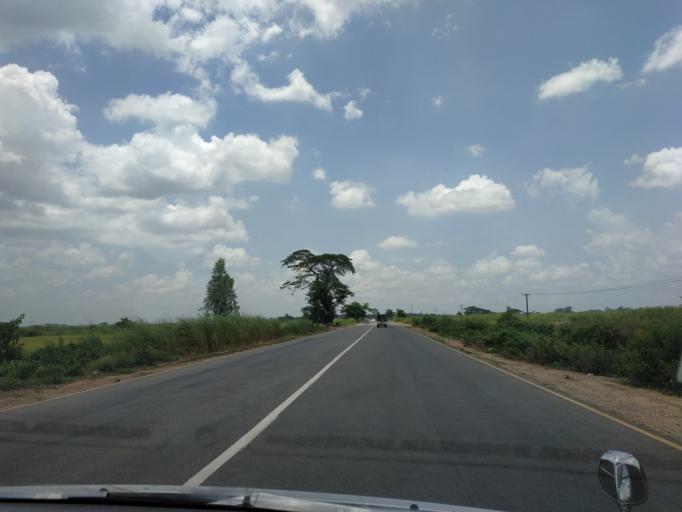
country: MM
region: Bago
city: Bago
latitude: 17.4696
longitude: 96.5615
